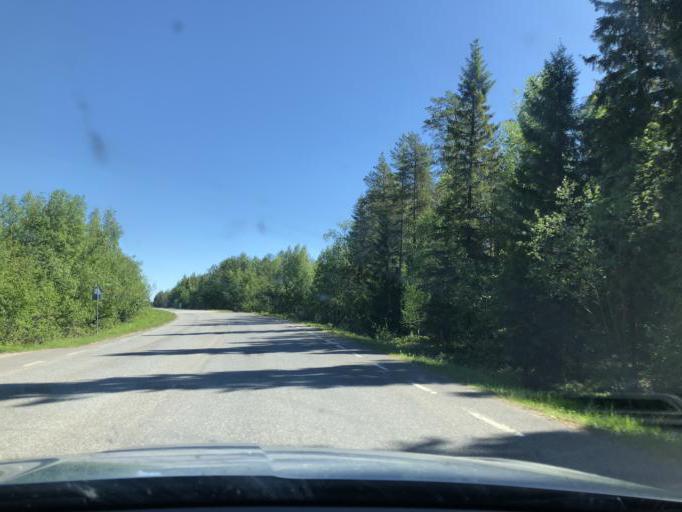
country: SE
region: Norrbotten
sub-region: Lulea Kommun
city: Gammelstad
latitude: 65.6605
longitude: 22.0592
